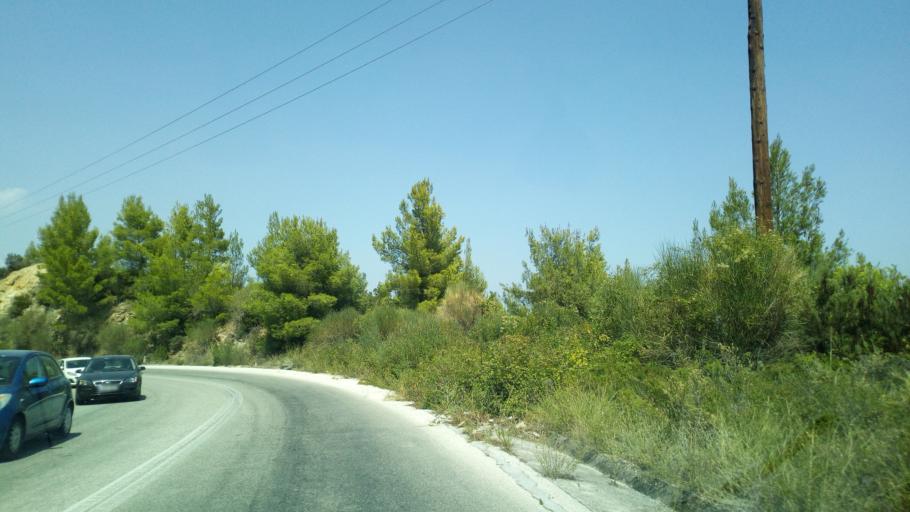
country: GR
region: Central Macedonia
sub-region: Nomos Chalkidikis
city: Neos Marmaras
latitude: 40.1644
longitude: 23.8659
